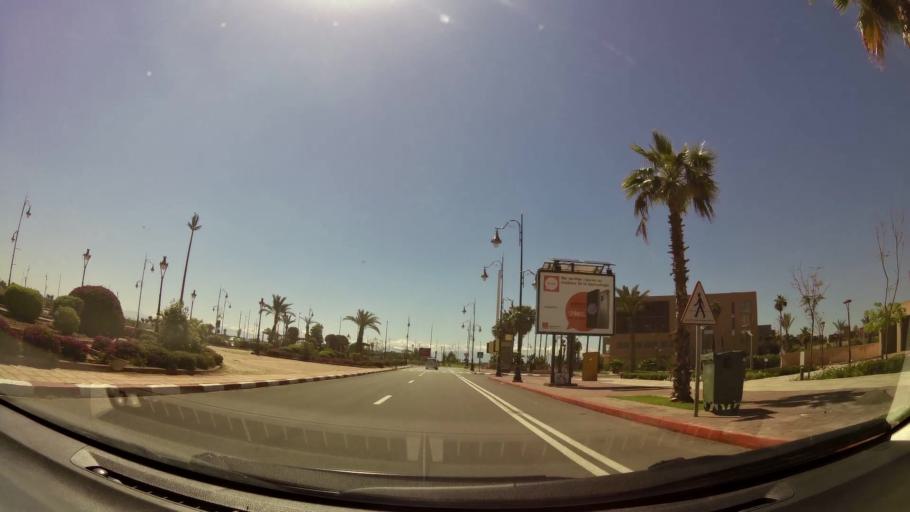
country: MA
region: Marrakech-Tensift-Al Haouz
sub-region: Marrakech
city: Marrakesh
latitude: 31.6053
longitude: -8.0001
